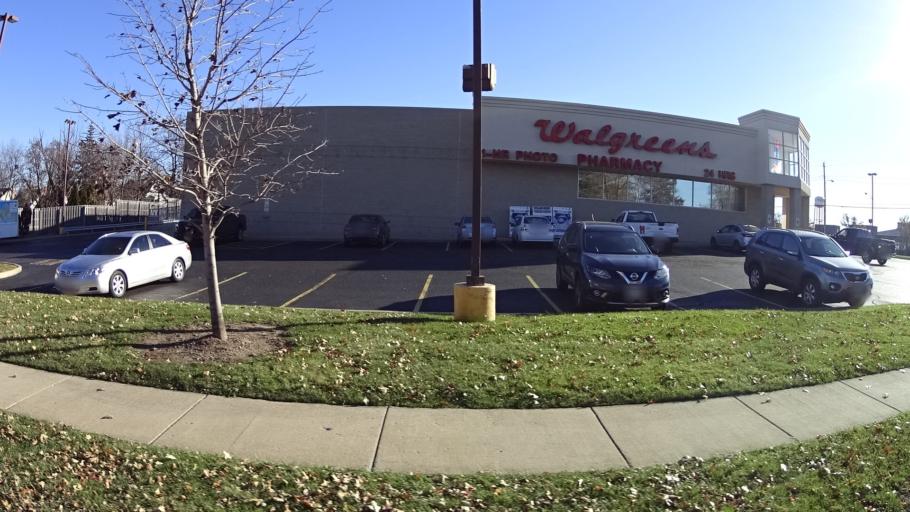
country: US
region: Ohio
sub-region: Lorain County
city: Elyria
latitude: 41.3732
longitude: -82.0942
